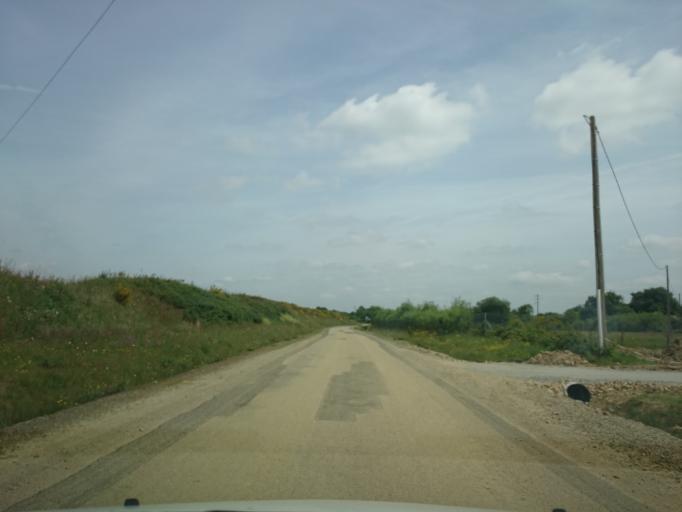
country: FR
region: Pays de la Loire
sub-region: Departement de la Loire-Atlantique
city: La Montagne
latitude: 47.1749
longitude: -1.6929
